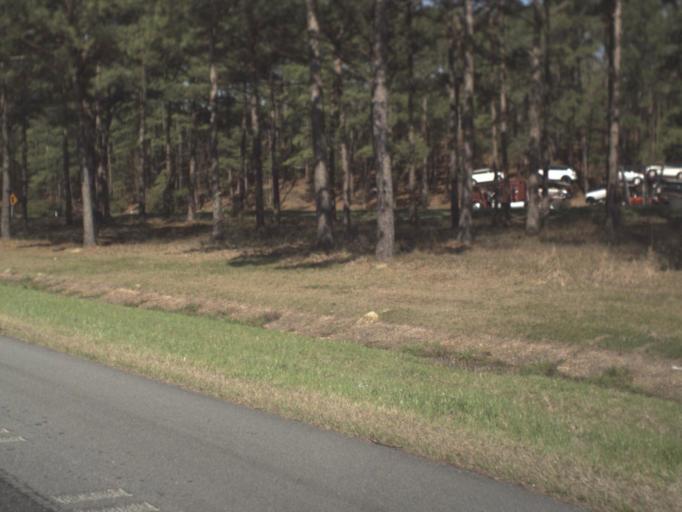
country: US
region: Florida
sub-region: Gadsden County
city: Chattahoochee
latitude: 30.6181
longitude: -84.8235
